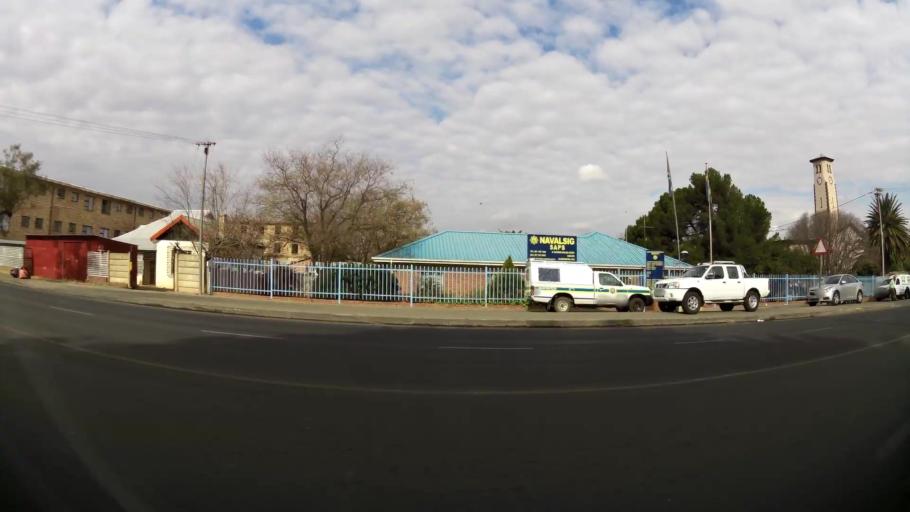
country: ZA
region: Orange Free State
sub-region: Mangaung Metropolitan Municipality
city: Bloemfontein
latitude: -29.1053
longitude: 26.2374
